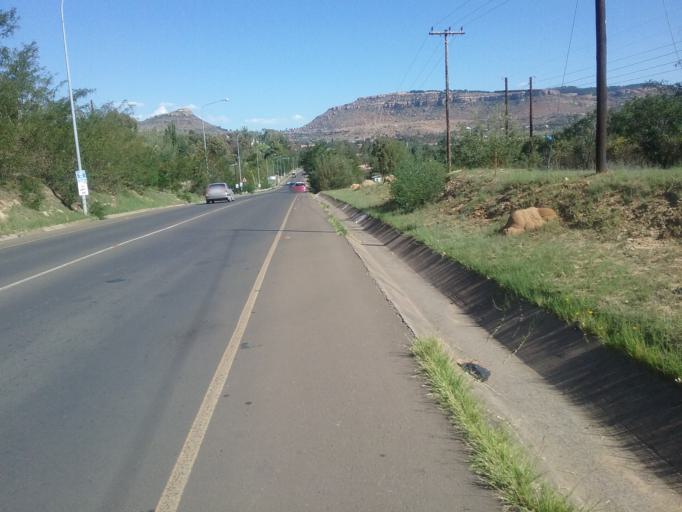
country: LS
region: Maseru
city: Maseru
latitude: -29.3110
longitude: 27.4673
